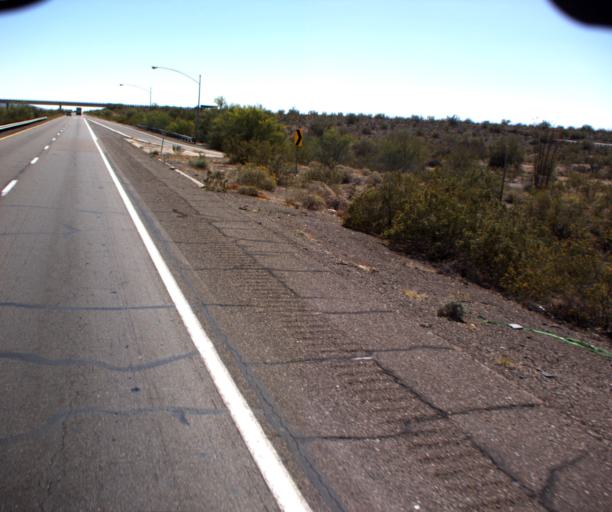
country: US
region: Arizona
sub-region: La Paz County
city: Quartzsite
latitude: 33.6620
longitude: -114.0158
